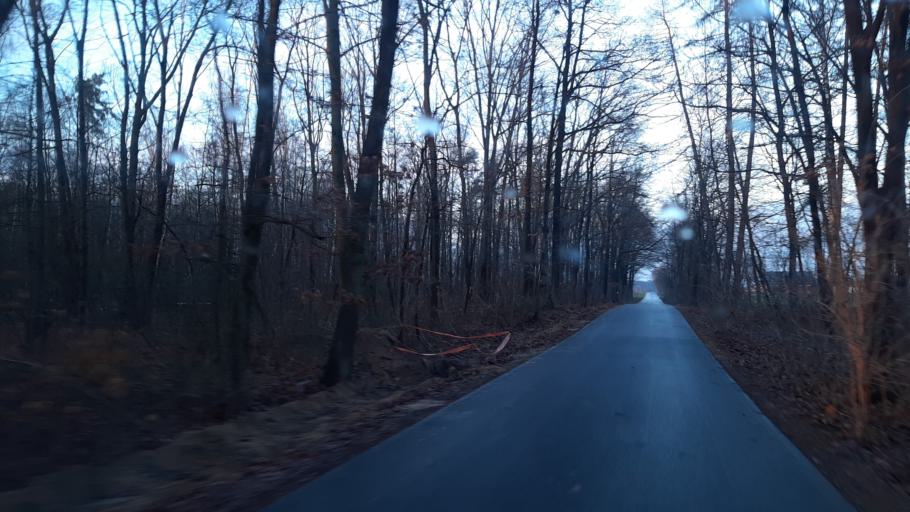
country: PL
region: Lublin Voivodeship
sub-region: Powiat lubelski
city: Garbow
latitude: 51.3743
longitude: 22.4003
